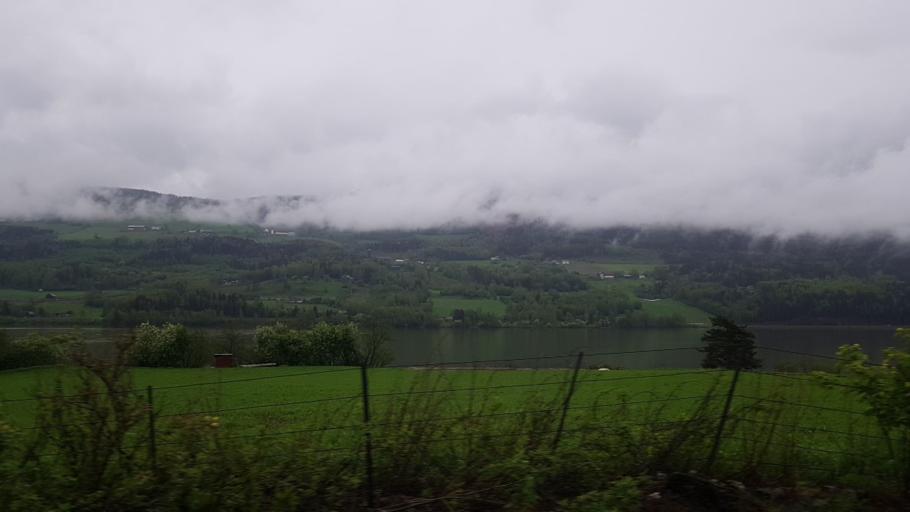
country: NO
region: Oppland
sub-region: Oyer
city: Tretten
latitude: 61.3375
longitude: 10.2868
